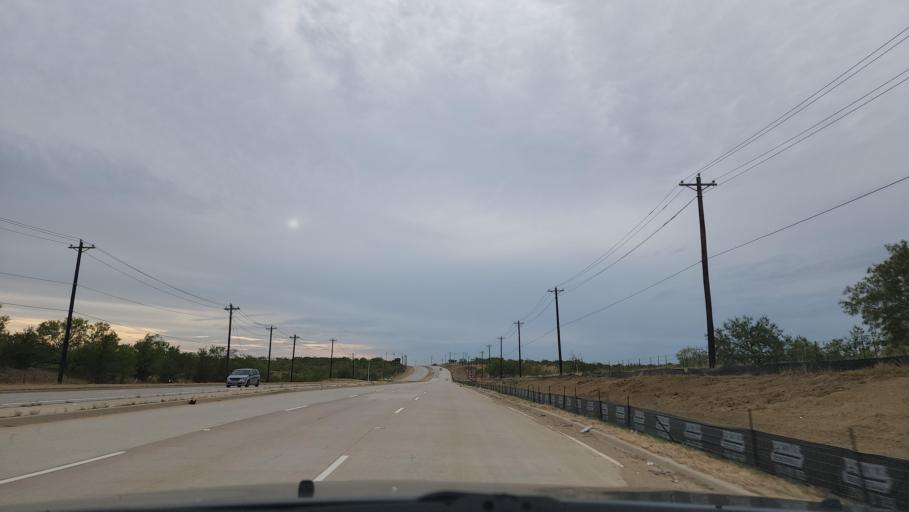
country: US
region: Texas
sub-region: Denton County
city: Roanoke
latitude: 33.0624
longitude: -97.2235
